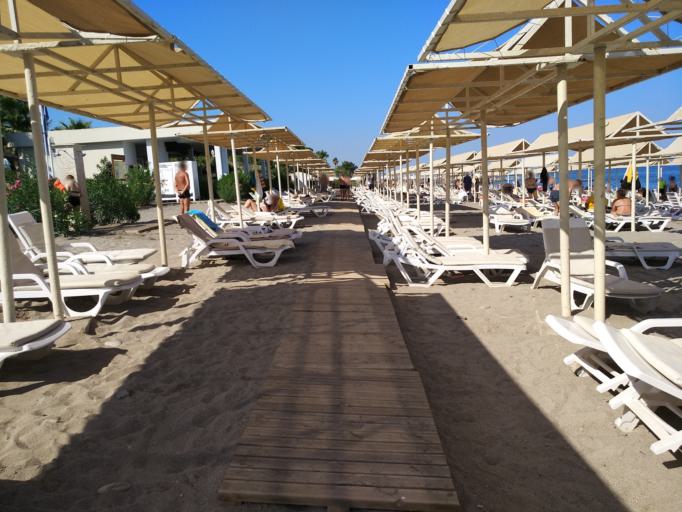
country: TR
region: Antalya
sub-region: Kemer
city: Goeynuek
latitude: 36.6650
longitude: 30.5631
